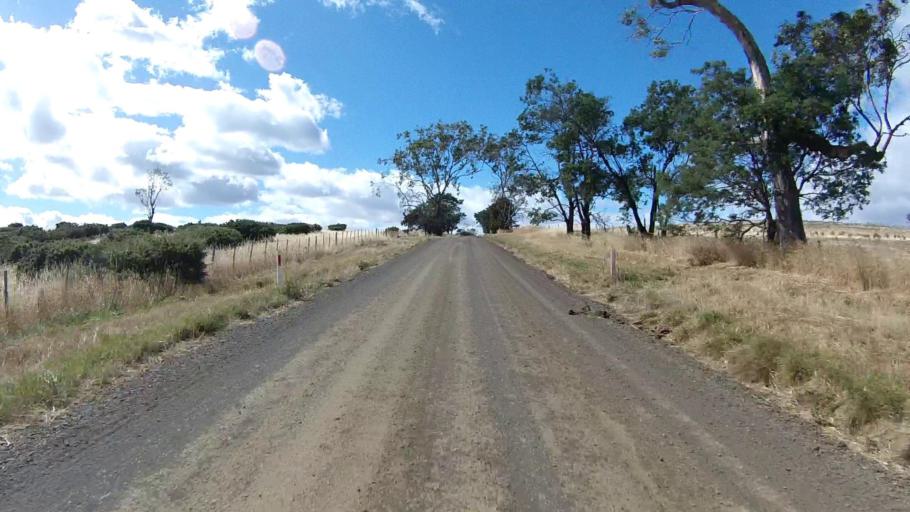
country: AU
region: Tasmania
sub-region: Northern Midlands
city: Evandale
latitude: -41.7231
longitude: 147.4338
